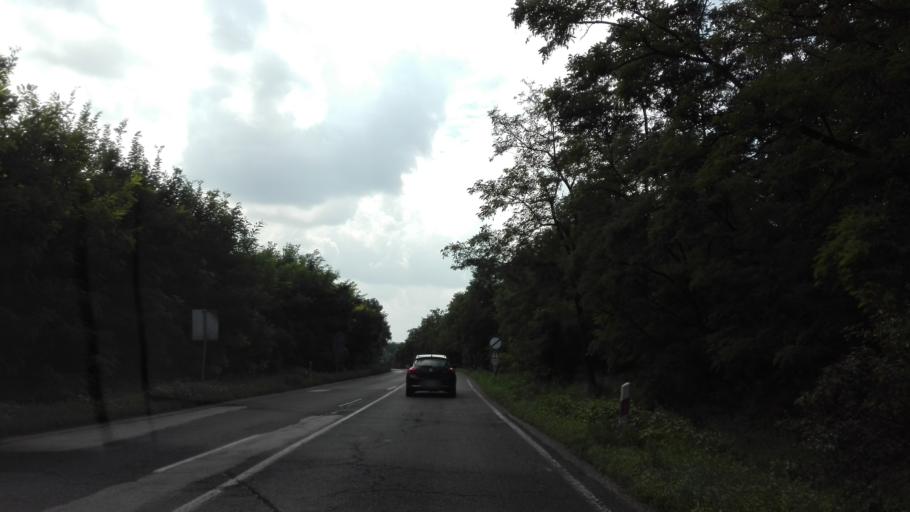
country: HU
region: Fejer
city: Cece
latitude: 46.7678
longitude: 18.6053
